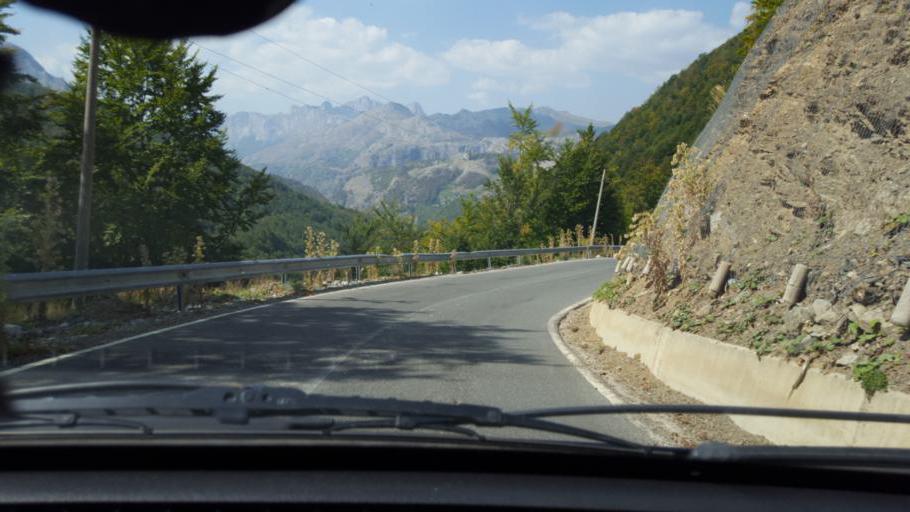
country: AL
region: Kukes
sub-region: Rrethi i Tropojes
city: Valbone
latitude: 42.5333
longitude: 19.7142
